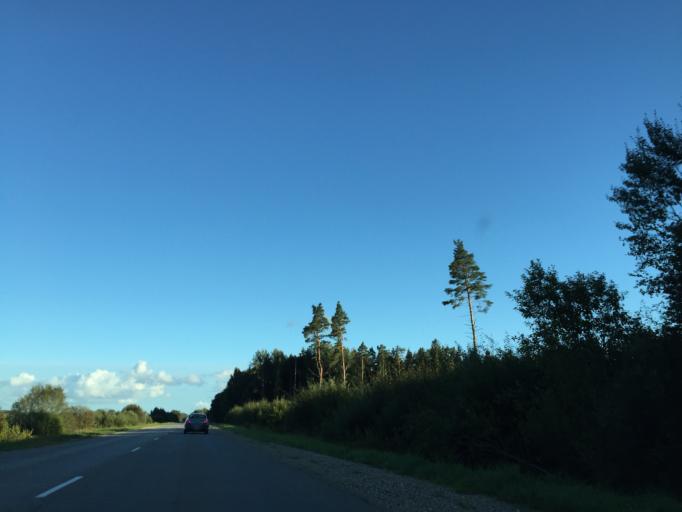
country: LV
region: Kuldigas Rajons
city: Kuldiga
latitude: 56.9528
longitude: 22.0103
